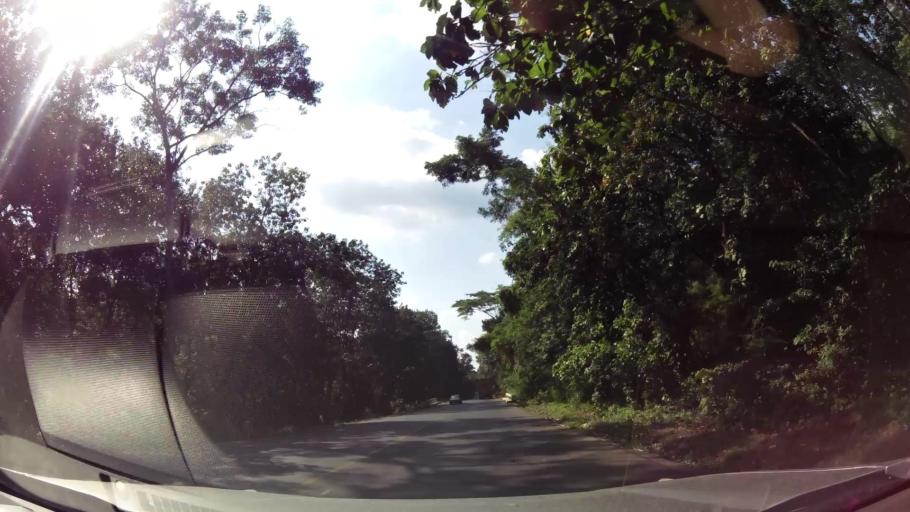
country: GT
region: Retalhuleu
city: San Sebastian
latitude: 14.5508
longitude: -91.6310
